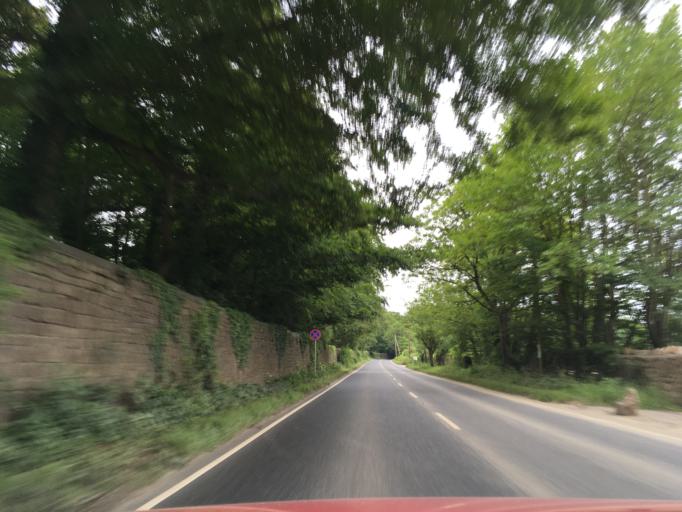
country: GB
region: England
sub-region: North Somerset
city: Long Ashton
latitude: 51.4474
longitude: -2.6595
